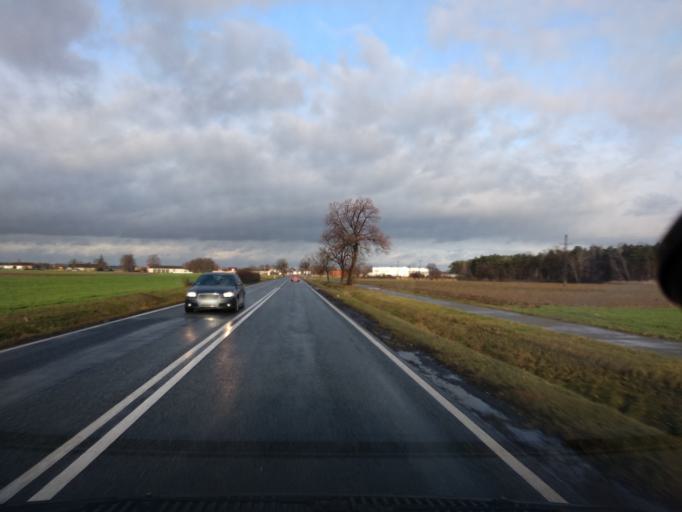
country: PL
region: Greater Poland Voivodeship
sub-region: Powiat koninski
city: Rychwal
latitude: 52.0893
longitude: 18.1642
